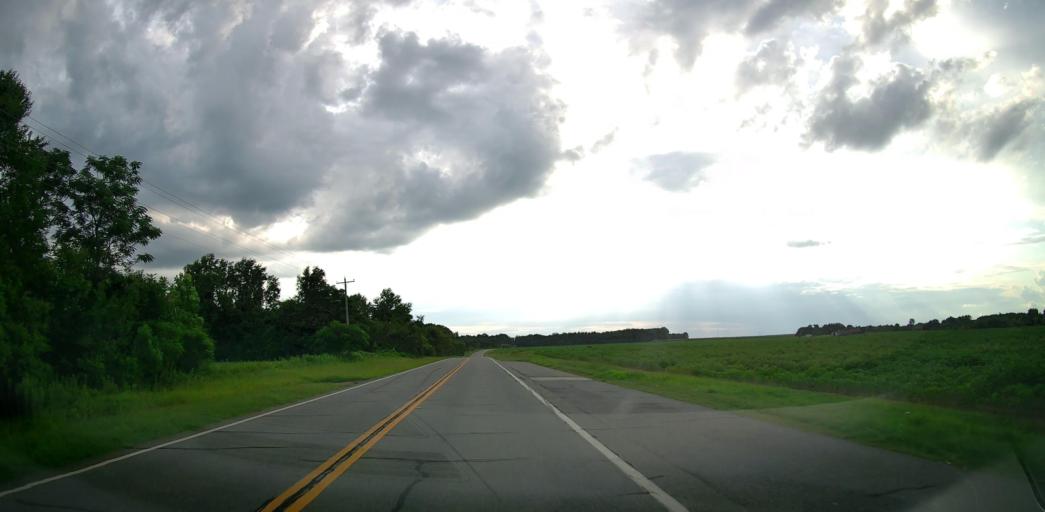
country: US
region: Georgia
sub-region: Pulaski County
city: Hawkinsville
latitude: 32.2959
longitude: -83.5372
